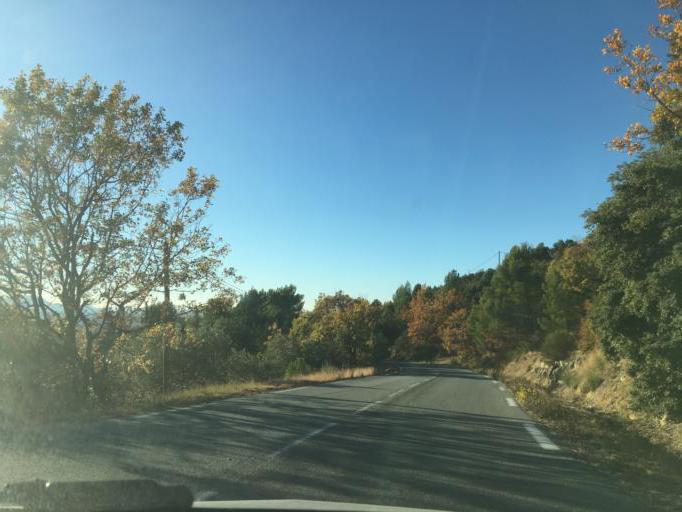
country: FR
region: Provence-Alpes-Cote d'Azur
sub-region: Departement du Var
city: Villecroze
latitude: 43.5925
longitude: 6.2956
